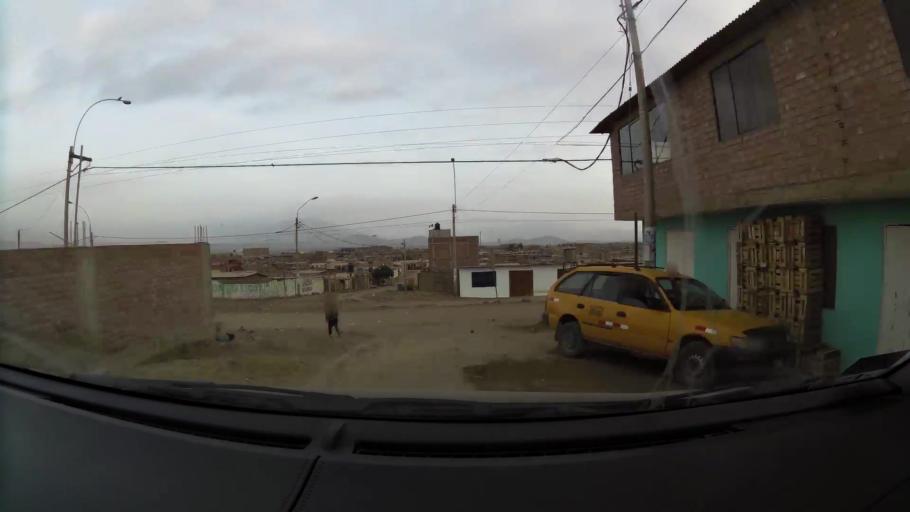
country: PE
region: Lima
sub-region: Lima
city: Santa Rosa
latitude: -11.7307
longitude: -77.1436
